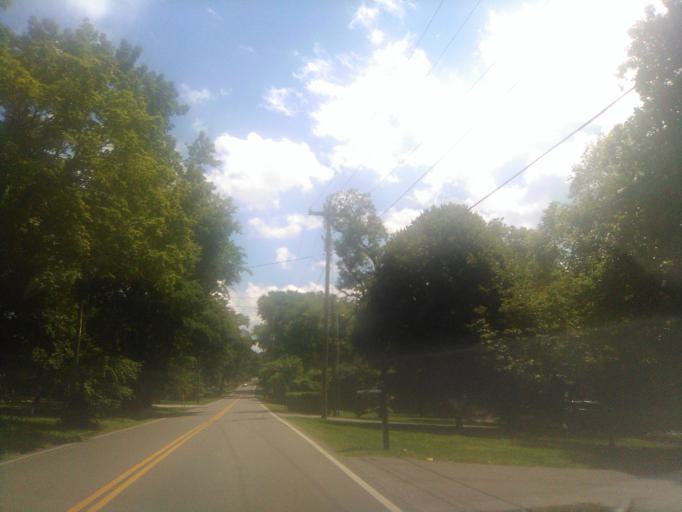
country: US
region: Tennessee
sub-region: Davidson County
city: Belle Meade
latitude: 36.1084
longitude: -86.8445
